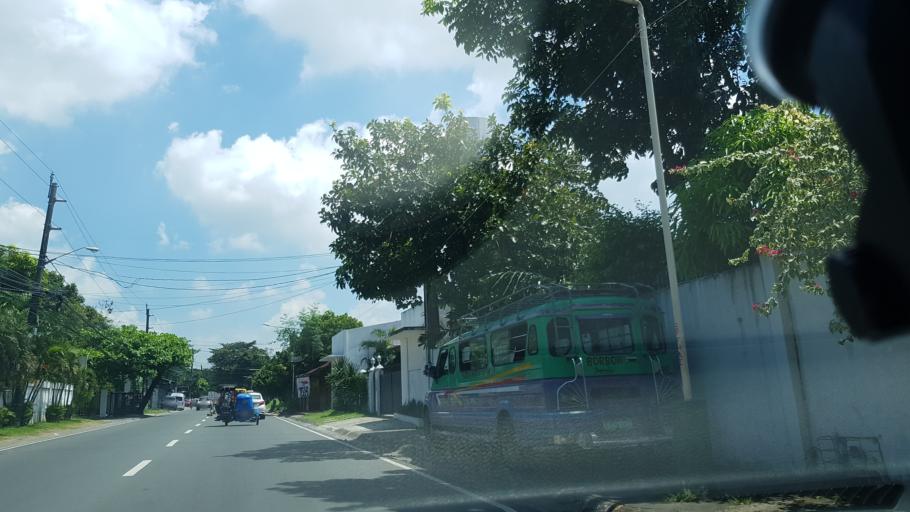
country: PH
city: Sambayanihan People's Village
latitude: 14.4491
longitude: 121.0075
